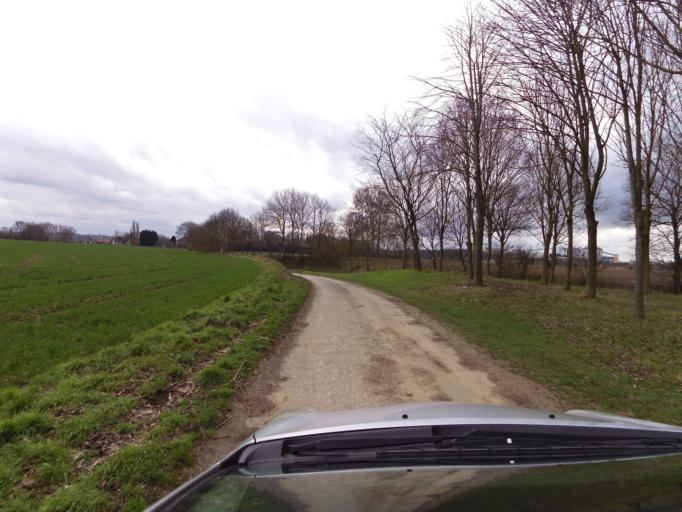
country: FR
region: Nord-Pas-de-Calais
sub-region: Departement du Pas-de-Calais
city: Agny
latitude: 50.2172
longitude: 2.7810
